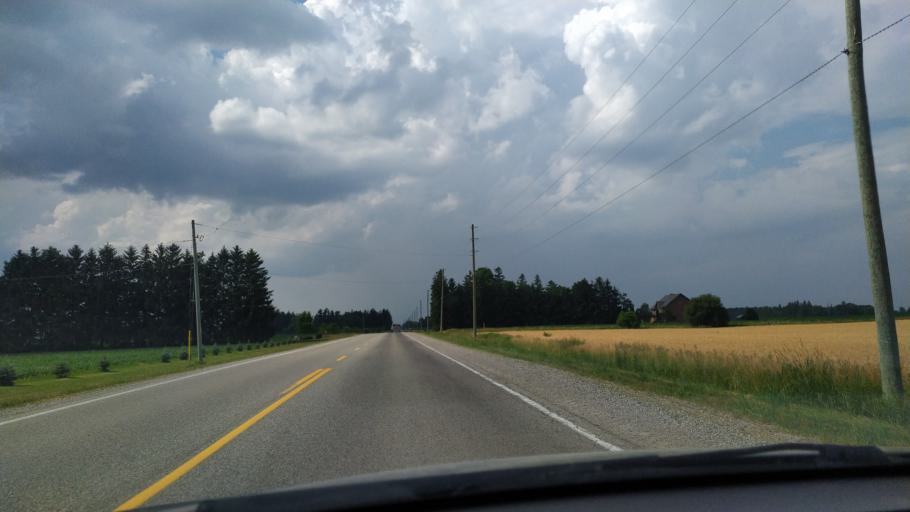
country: CA
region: Ontario
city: London
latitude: 43.1200
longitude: -81.1662
